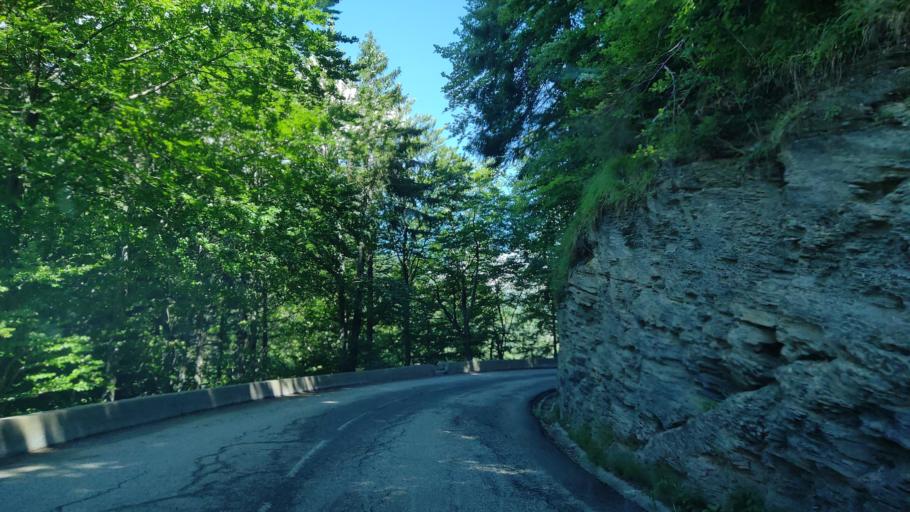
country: FR
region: Rhone-Alpes
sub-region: Departement de la Haute-Savoie
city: Praz-sur-Arly
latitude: 45.8264
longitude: 6.5101
